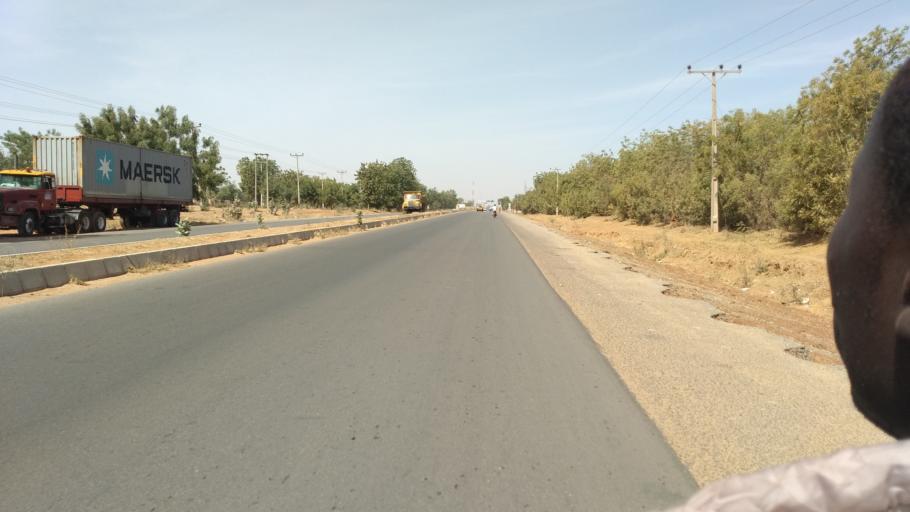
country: NG
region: Jigawa
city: Dutse
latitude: 11.6809
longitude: 9.3402
